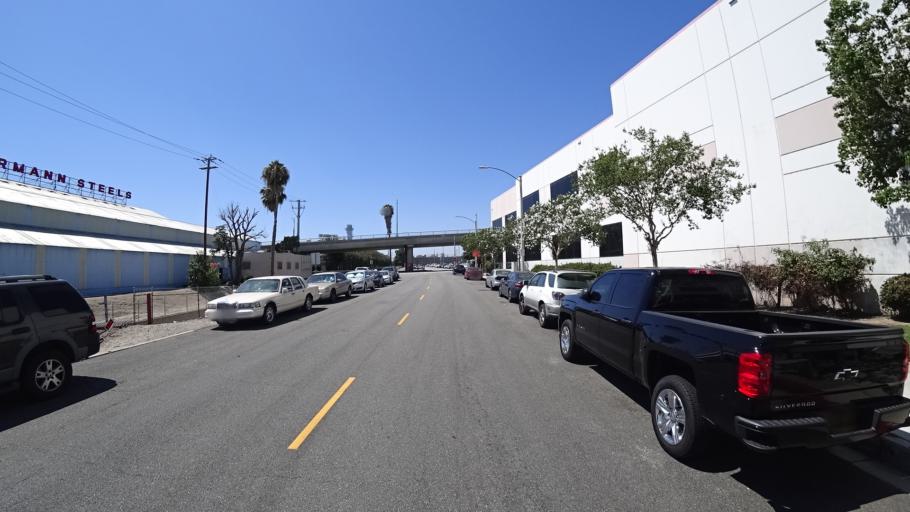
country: US
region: California
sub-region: Los Angeles County
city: Burbank
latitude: 34.1771
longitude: -118.3114
